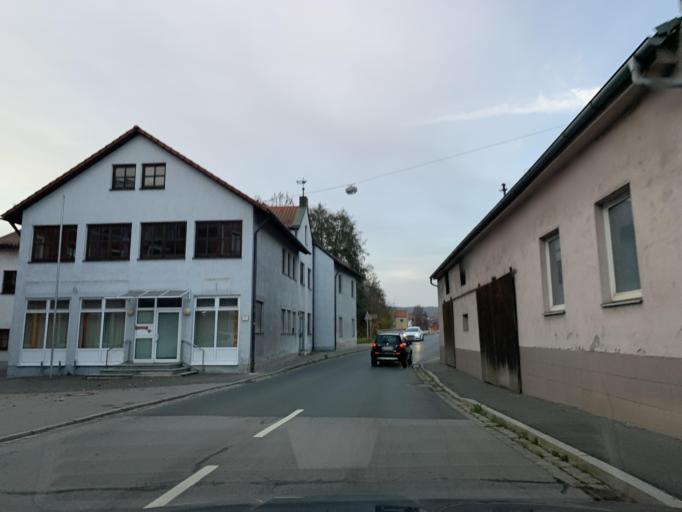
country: DE
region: Bavaria
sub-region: Upper Palatinate
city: Neunburg vorm Wald
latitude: 49.3492
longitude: 12.3820
